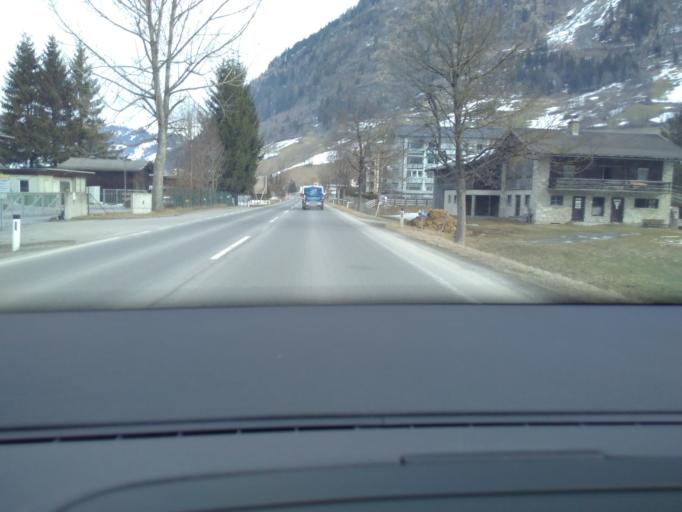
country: AT
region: Salzburg
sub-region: Politischer Bezirk Sankt Johann im Pongau
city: Bad Hofgastein
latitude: 47.1747
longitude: 13.0996
